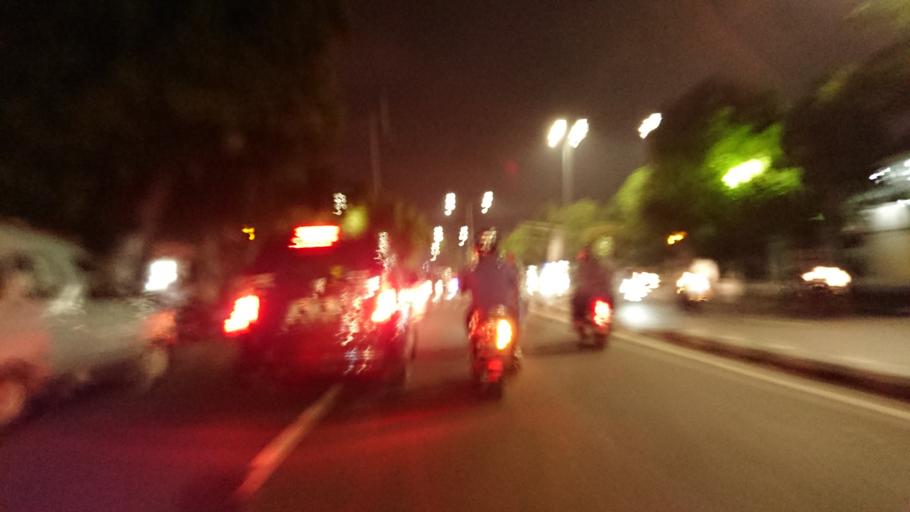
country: ID
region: Jakarta Raya
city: Jakarta
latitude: -6.1894
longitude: 106.8066
